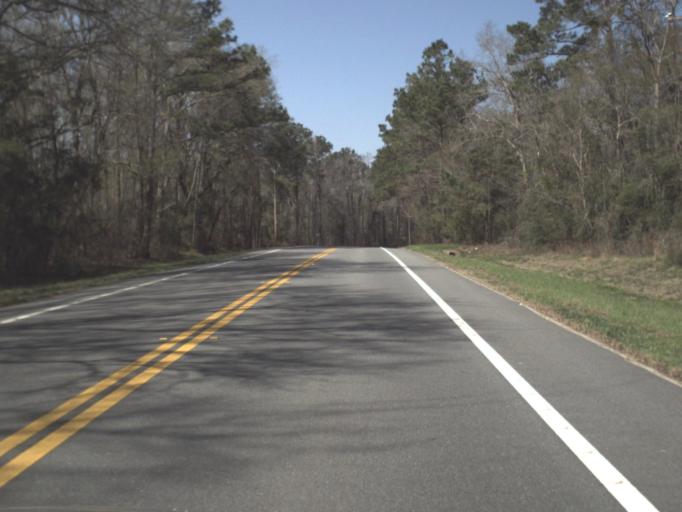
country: US
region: Florida
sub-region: Jackson County
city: Sneads
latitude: 30.6333
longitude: -85.0340
